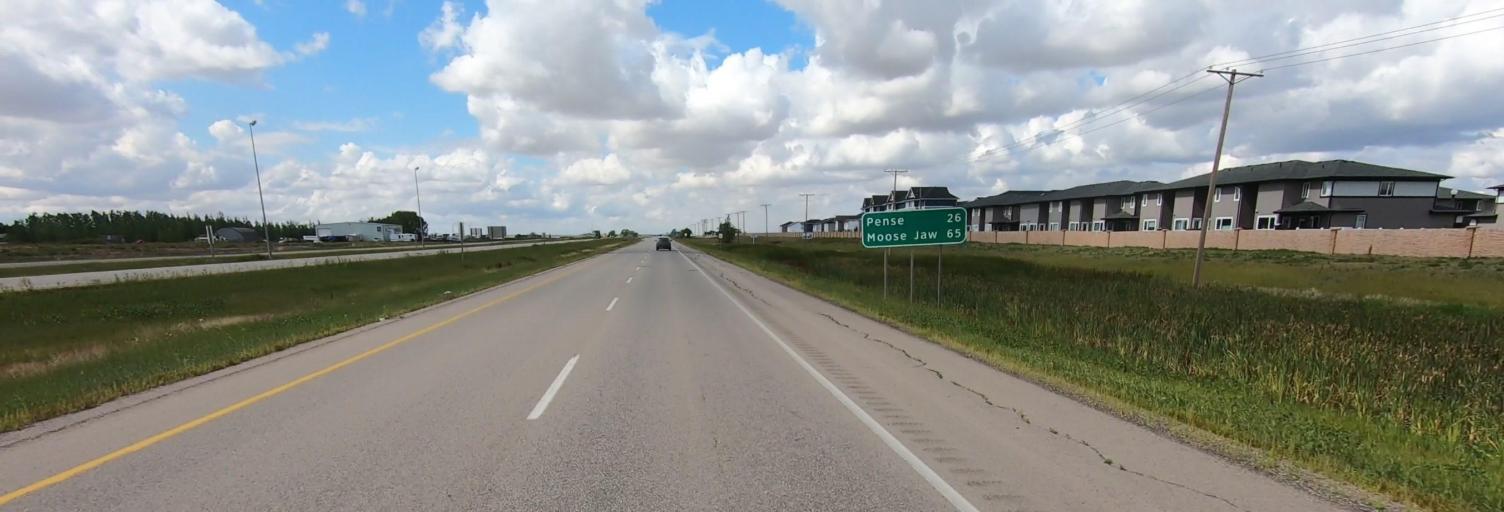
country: CA
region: Saskatchewan
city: Regina
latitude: 50.3971
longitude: -104.6550
